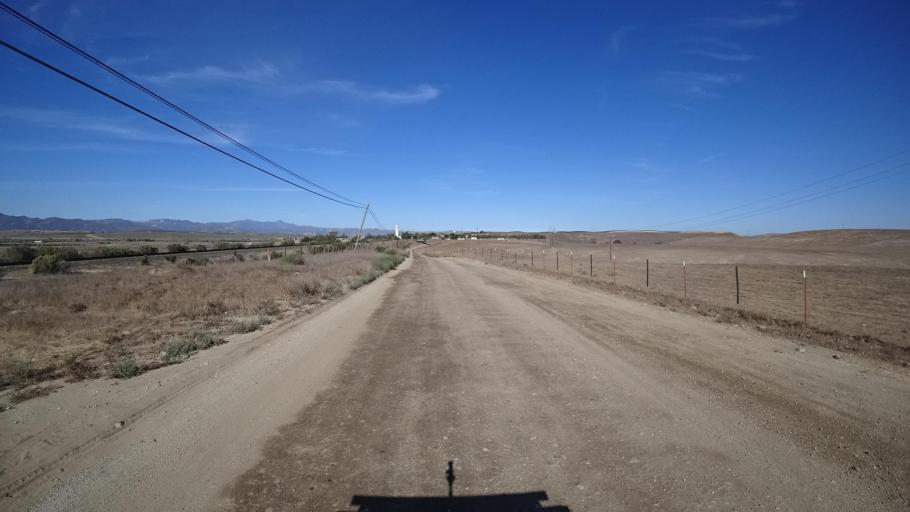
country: US
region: California
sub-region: Monterey County
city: King City
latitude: 36.1251
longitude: -121.0096
